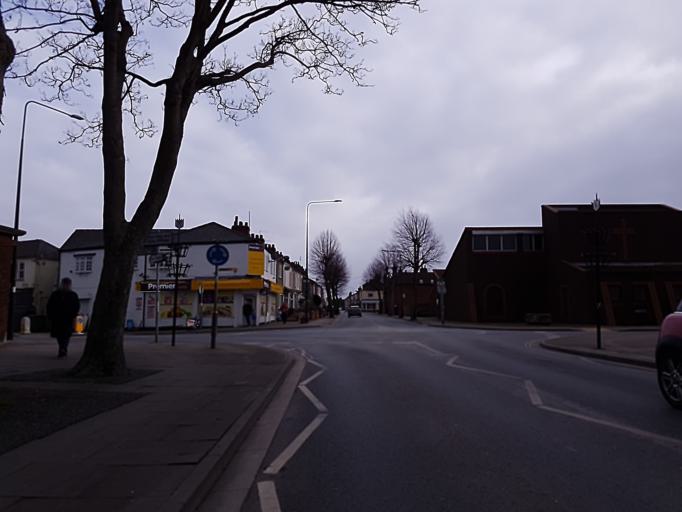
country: GB
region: England
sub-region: North East Lincolnshire
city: Cleethorpes
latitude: 53.5578
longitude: -0.0299
